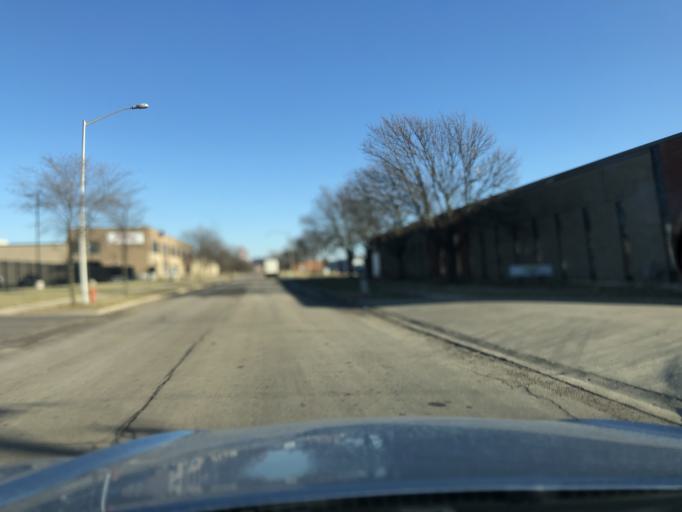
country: US
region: Illinois
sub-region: DuPage County
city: Itasca
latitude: 41.9859
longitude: -88.0405
